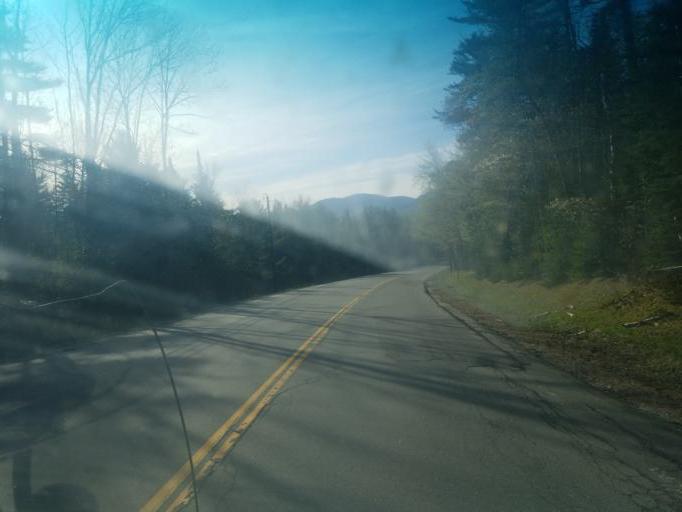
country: US
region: New Hampshire
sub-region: Grafton County
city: Deerfield
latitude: 44.2812
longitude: -71.6495
